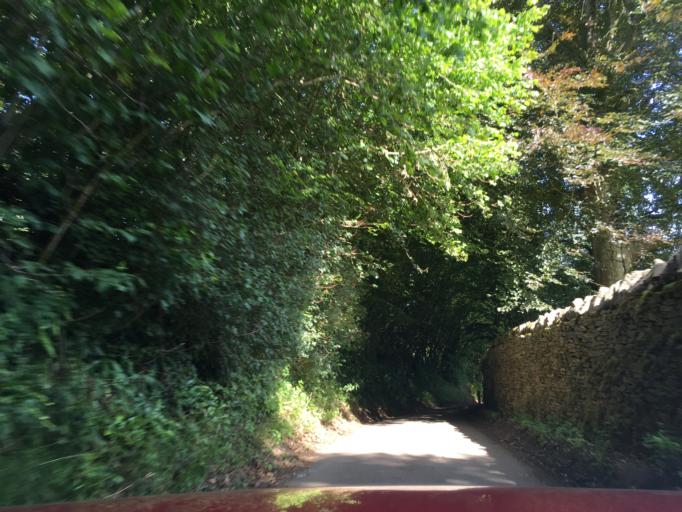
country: GB
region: England
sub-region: Wiltshire
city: Nettleton
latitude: 51.4934
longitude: -2.2706
